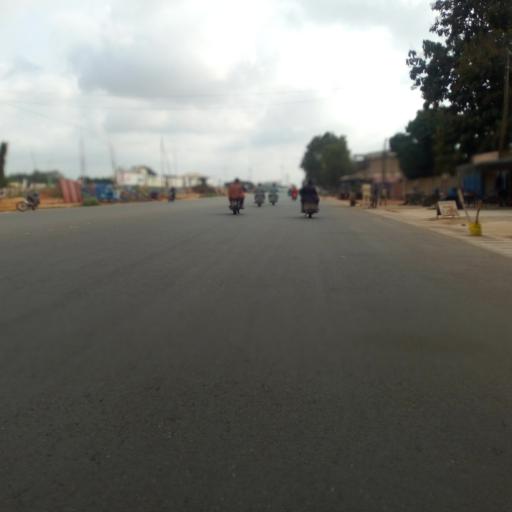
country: TG
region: Maritime
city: Lome
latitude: 6.1920
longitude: 1.2378
